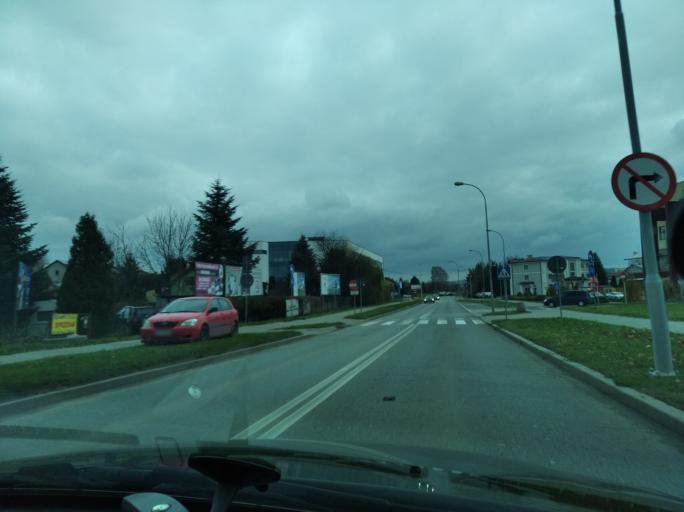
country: PL
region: Subcarpathian Voivodeship
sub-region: Rzeszow
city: Rzeszow
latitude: 50.0320
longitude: 22.0382
